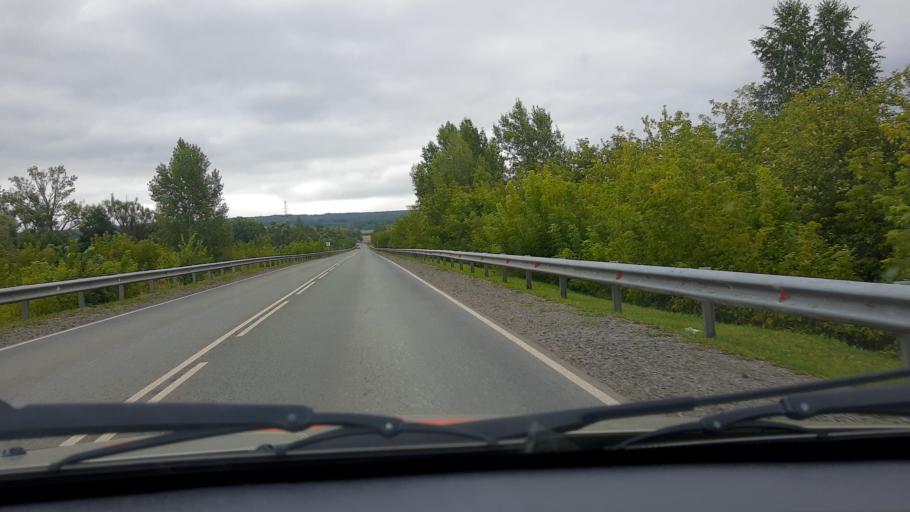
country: RU
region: Bashkortostan
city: Chishmy
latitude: 54.5697
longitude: 55.4669
